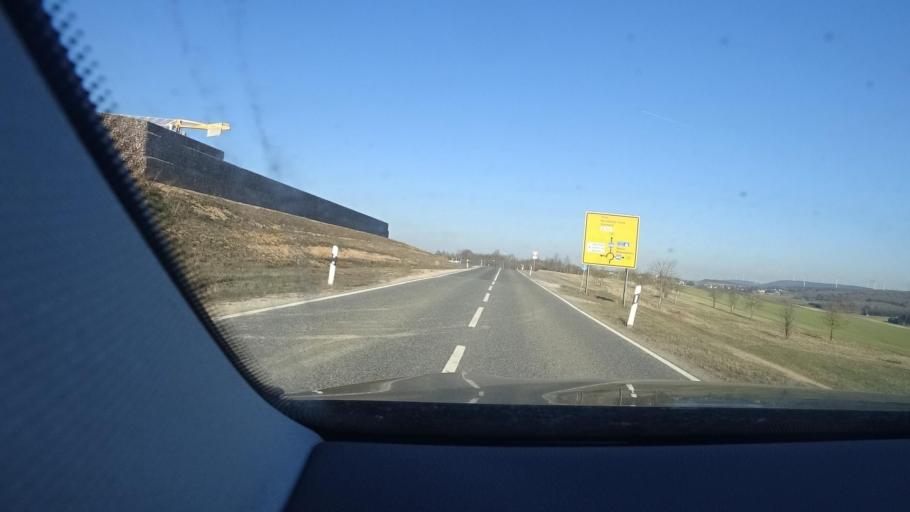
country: DE
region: Rheinland-Pfalz
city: Riesweiler
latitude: 49.9656
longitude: 7.5624
